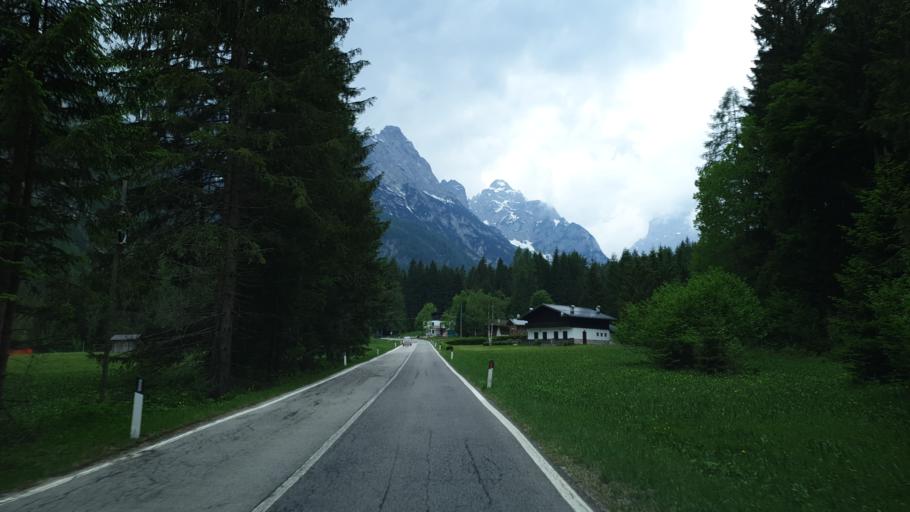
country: IT
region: Veneto
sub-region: Provincia di Belluno
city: Auronzo
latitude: 46.5477
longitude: 12.3267
